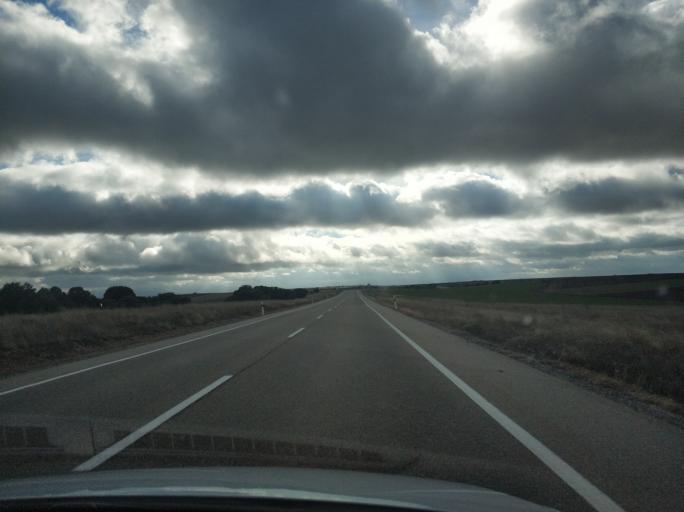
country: ES
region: Castille and Leon
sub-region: Provincia de Soria
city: Fuentecambron
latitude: 41.4802
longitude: -3.3184
